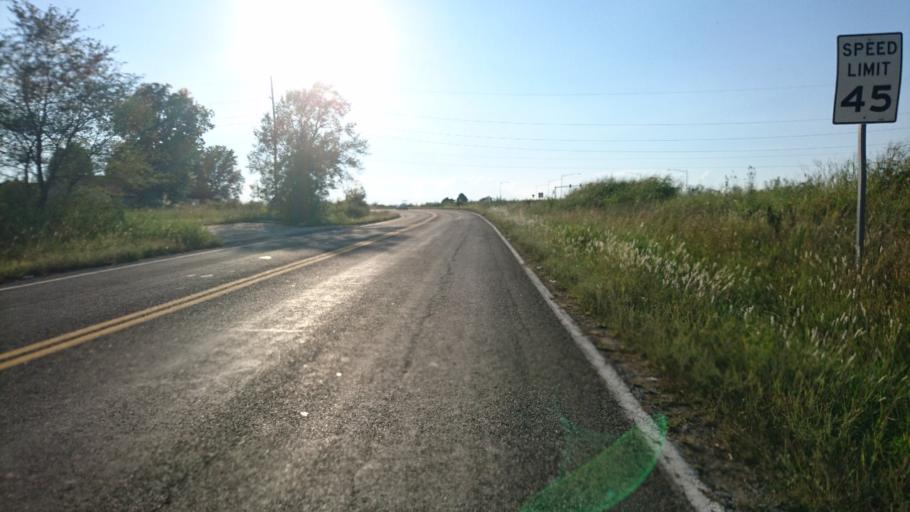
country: US
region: Missouri
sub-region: Greene County
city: Springfield
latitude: 37.2122
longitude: -93.3816
